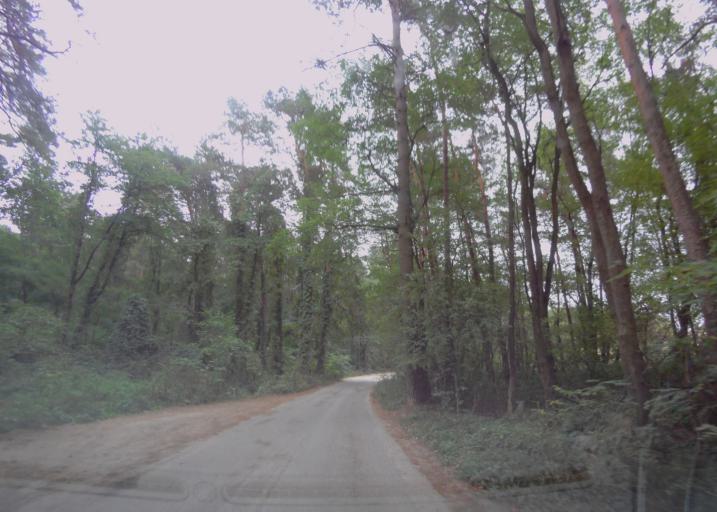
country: PL
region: Lublin Voivodeship
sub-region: Powiat krasnostawski
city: Krasnystaw
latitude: 50.9985
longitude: 23.1892
